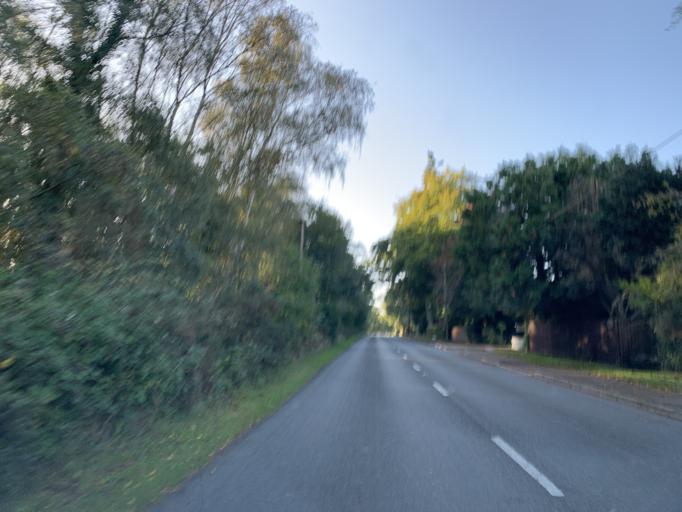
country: GB
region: England
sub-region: Wiltshire
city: Whiteparish
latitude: 50.9650
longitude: -1.6335
